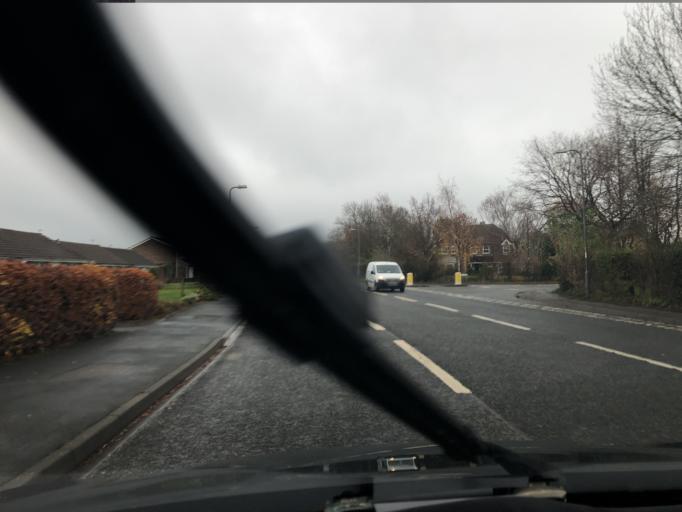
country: GB
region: England
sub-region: North Yorkshire
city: Stokesley
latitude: 54.4778
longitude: -1.1879
